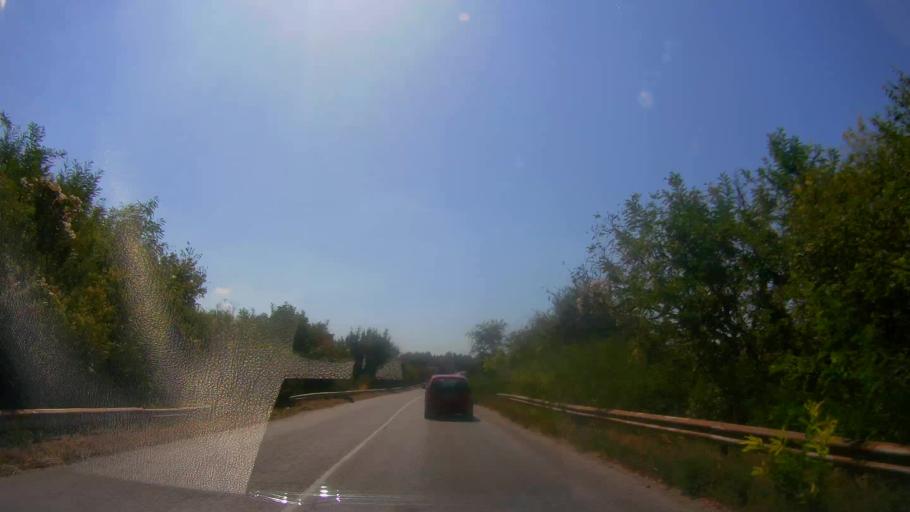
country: BG
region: Veliko Turnovo
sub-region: Obshtina Polski Trumbesh
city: Polski Trumbesh
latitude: 43.2699
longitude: 25.6436
